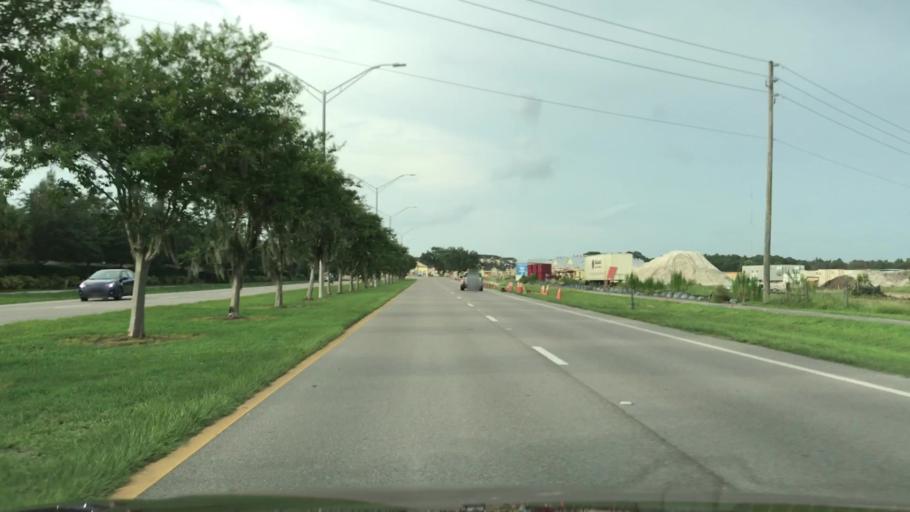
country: US
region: Florida
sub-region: Sarasota County
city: Venice Gardens
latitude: 27.0935
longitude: -82.3871
